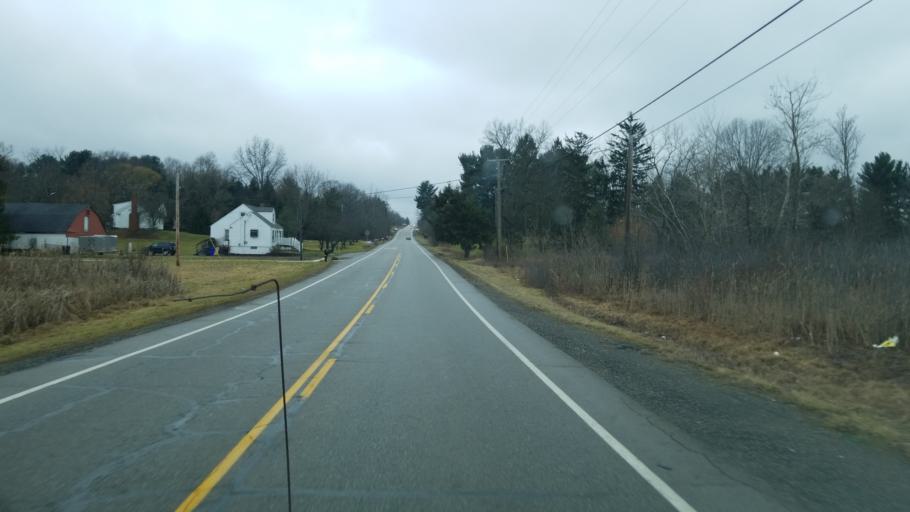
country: US
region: Ohio
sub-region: Portage County
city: Streetsboro
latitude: 41.2399
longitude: -81.3813
